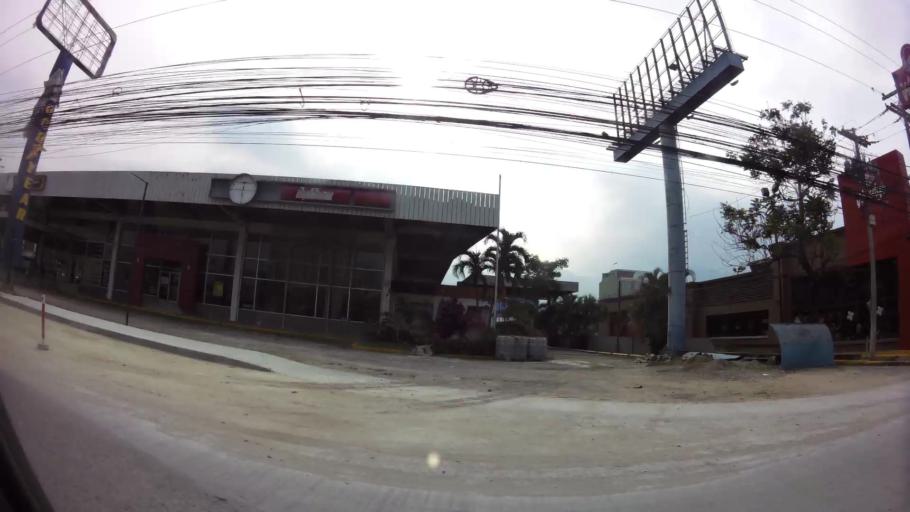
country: HN
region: Cortes
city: San Pedro Sula
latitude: 15.5216
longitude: -88.0250
